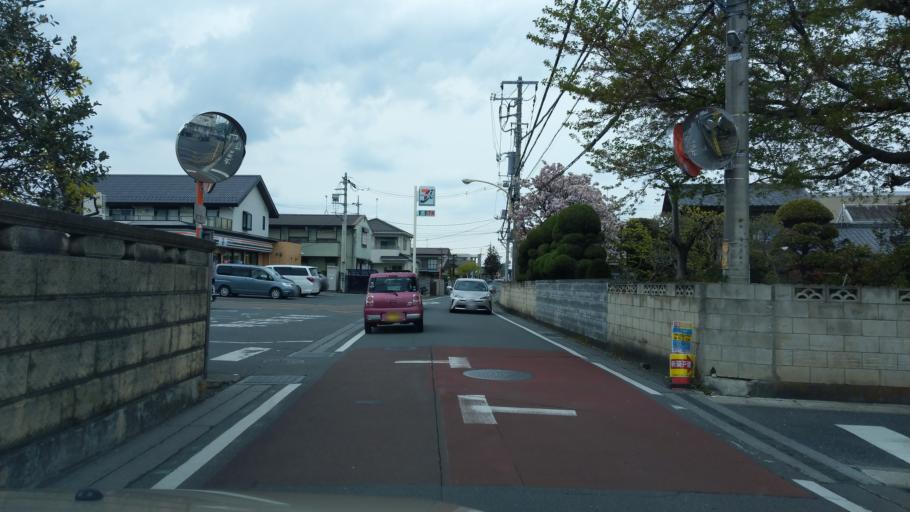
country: JP
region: Saitama
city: Yono
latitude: 35.9126
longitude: 139.5899
